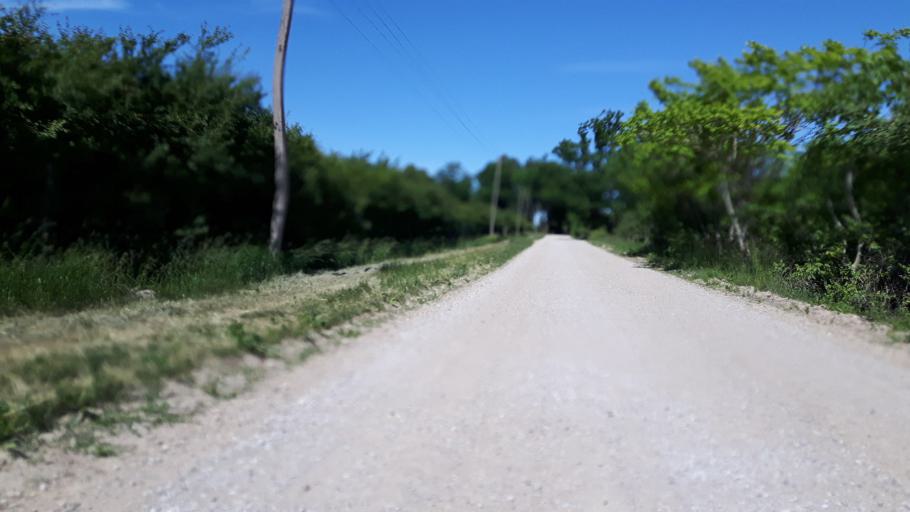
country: LV
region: Kandava
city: Kandava
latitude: 57.0421
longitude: 22.8795
